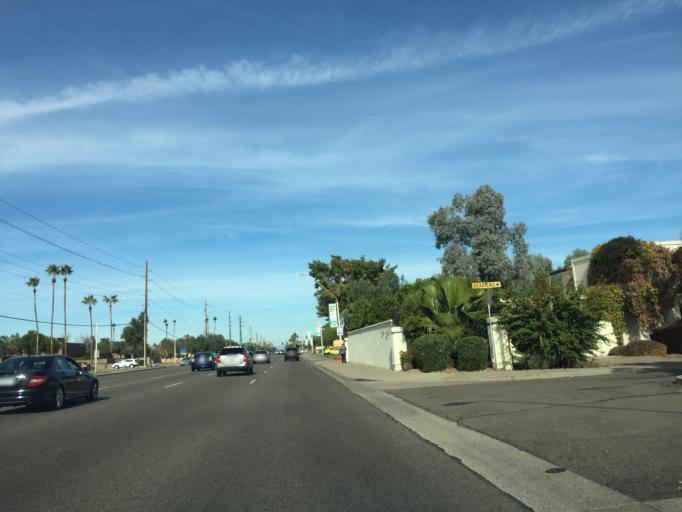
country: US
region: Arizona
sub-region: Maricopa County
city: Tempe Junction
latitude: 33.3900
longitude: -111.9263
